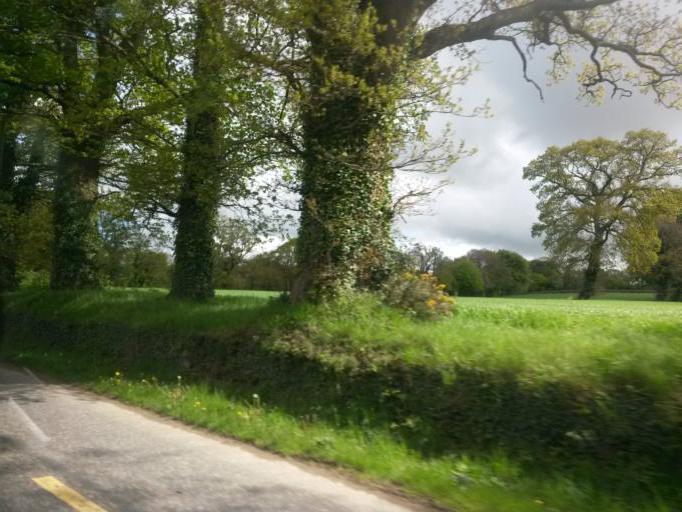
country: IE
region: Leinster
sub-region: Loch Garman
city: Enniscorthy
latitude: 52.4607
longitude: -6.5590
